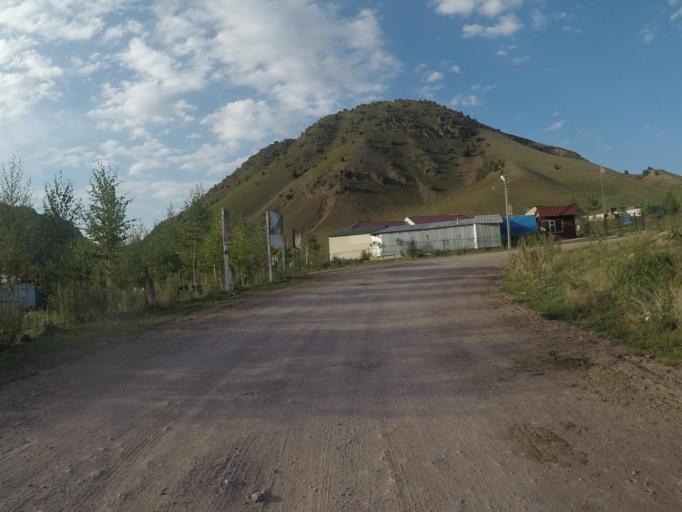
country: KG
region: Chuy
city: Bishkek
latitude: 42.6411
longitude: 74.6202
